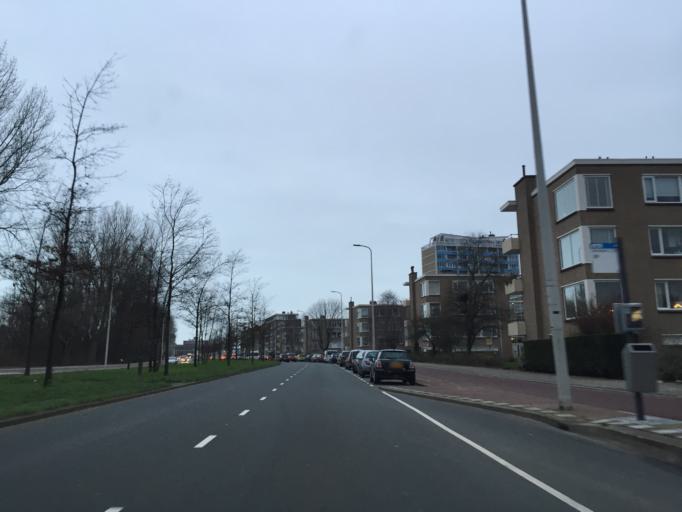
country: NL
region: South Holland
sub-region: Gemeente Westland
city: Poeldijk
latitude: 52.0630
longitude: 4.2265
